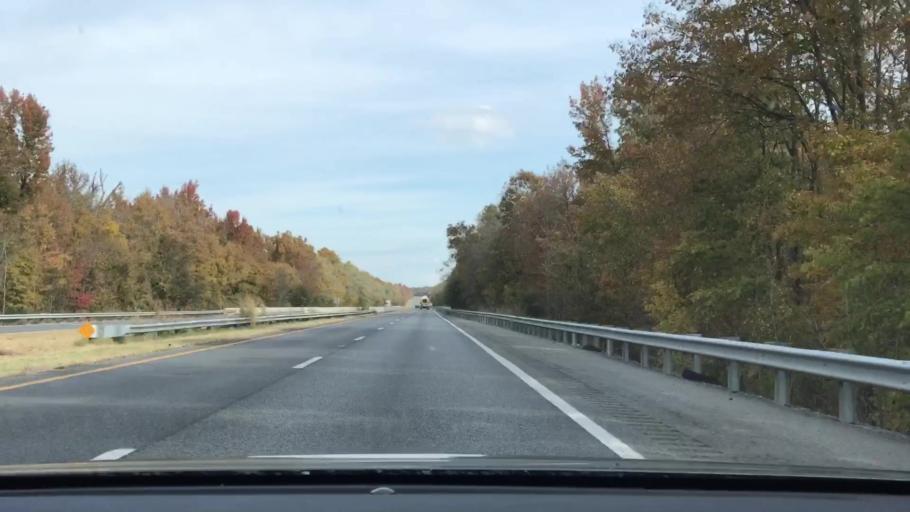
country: US
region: Kentucky
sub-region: Marshall County
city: Benton
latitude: 36.8774
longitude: -88.3598
